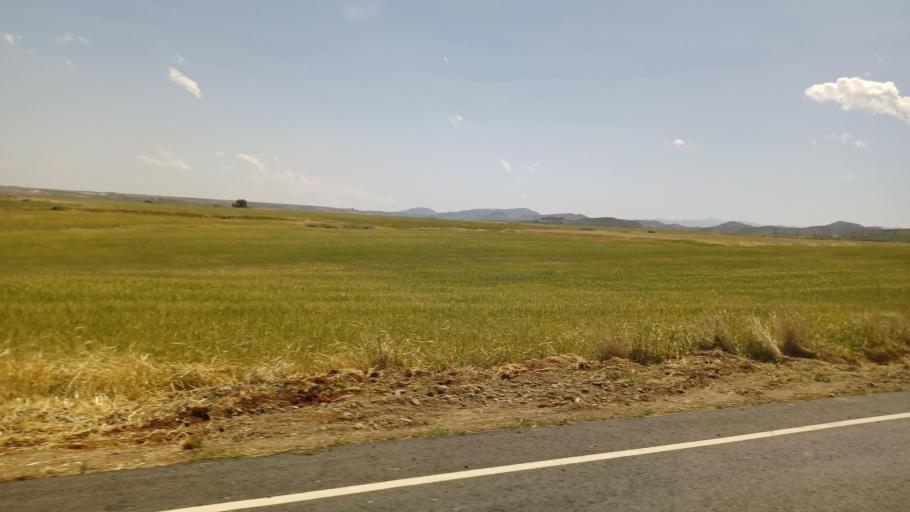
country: CY
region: Lefkosia
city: Astromeritis
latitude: 35.0999
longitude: 33.0146
